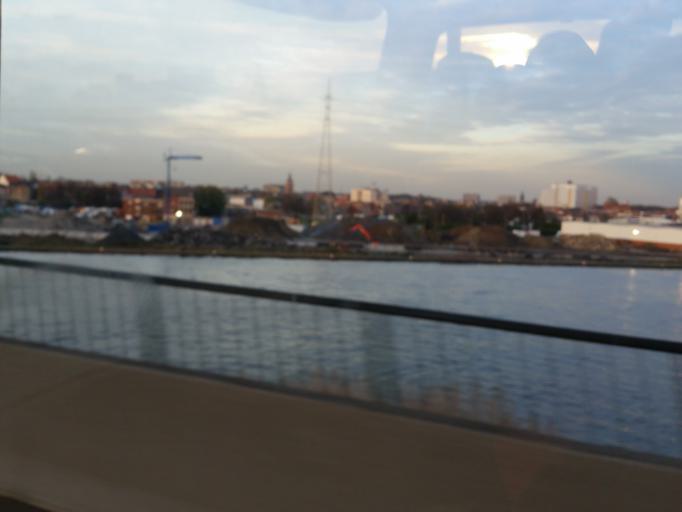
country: BE
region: Flanders
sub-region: Provincie Antwerpen
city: Antwerpen
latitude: 51.2334
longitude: 4.4364
